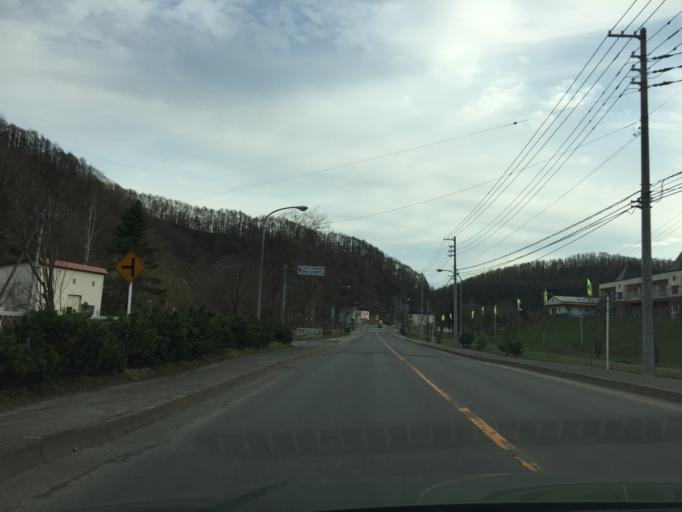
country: JP
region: Hokkaido
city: Utashinai
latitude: 43.5204
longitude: 142.0307
